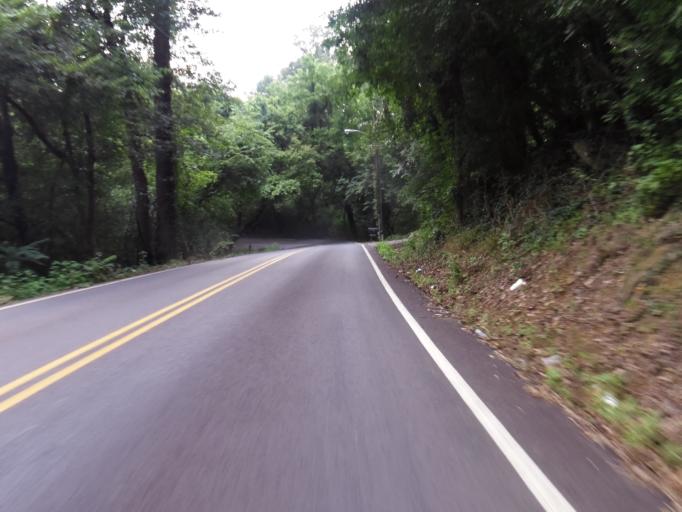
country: US
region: Tennessee
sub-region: Knox County
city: Knoxville
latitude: 35.9704
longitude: -83.8752
